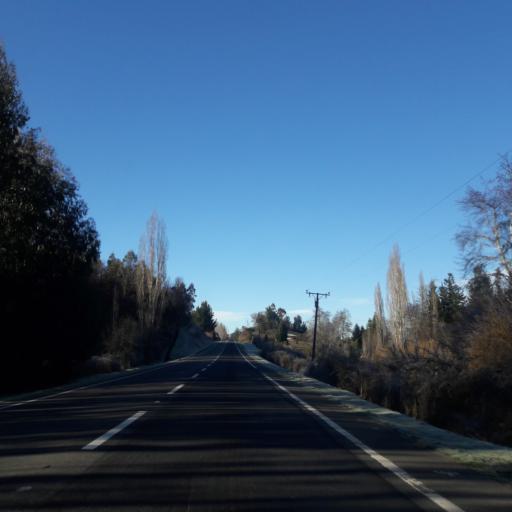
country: CL
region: Biobio
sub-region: Provincia de Biobio
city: La Laja
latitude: -37.3204
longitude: -72.9197
